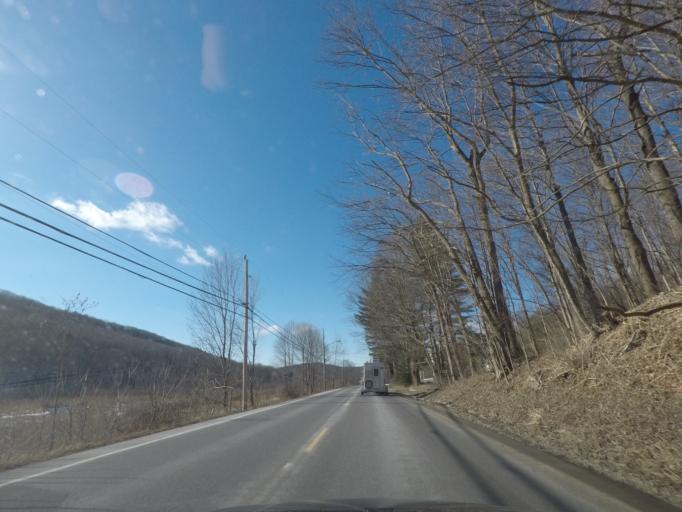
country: US
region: Massachusetts
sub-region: Berkshire County
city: Richmond
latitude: 42.4148
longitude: -73.4530
